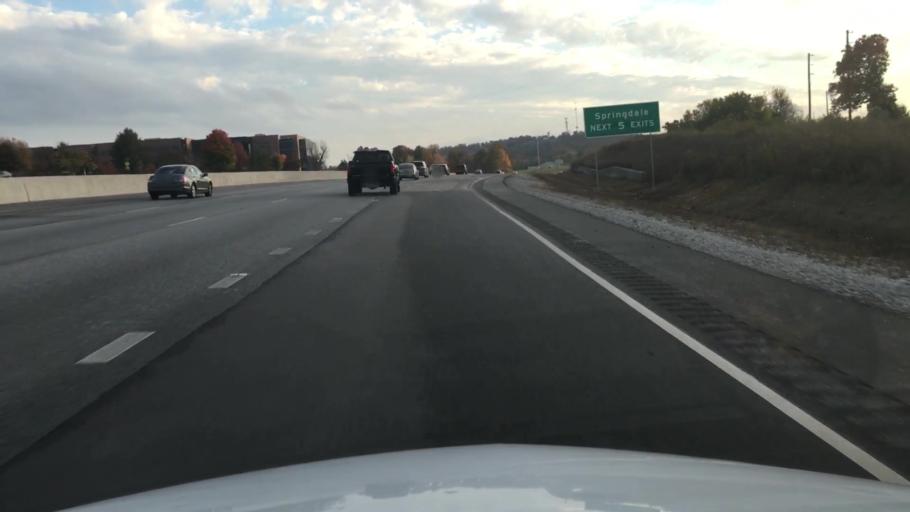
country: US
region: Arkansas
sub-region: Benton County
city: Lowell
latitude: 36.2484
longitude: -94.1508
